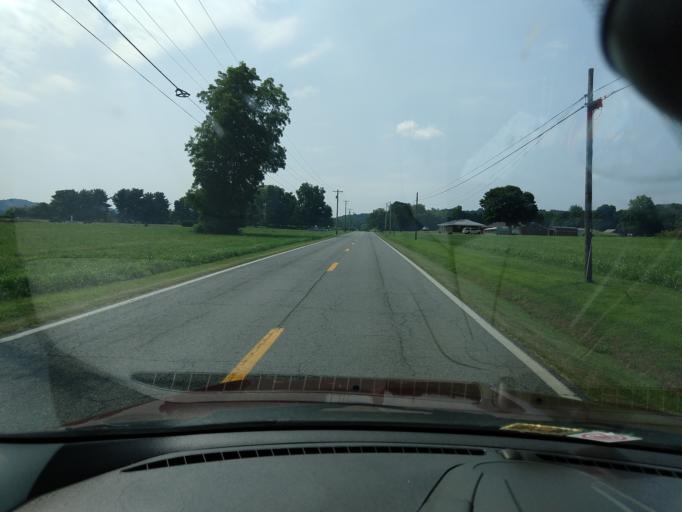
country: US
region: West Virginia
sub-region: Mason County
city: New Haven
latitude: 38.9432
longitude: -81.9194
